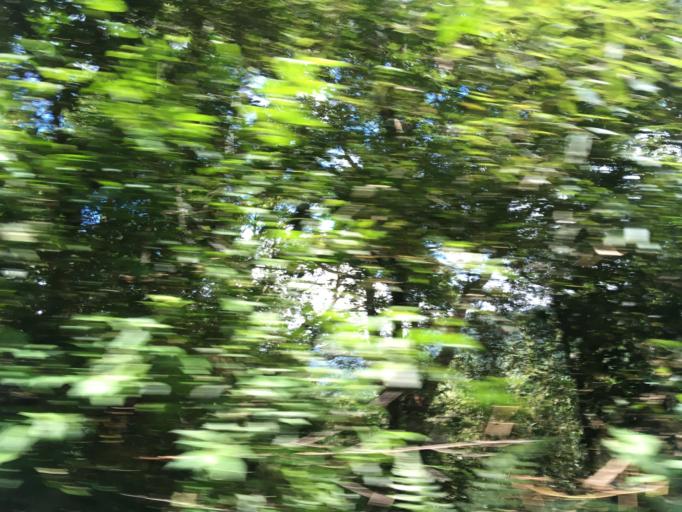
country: TW
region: Taipei
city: Taipei
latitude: 24.9398
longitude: 121.5776
